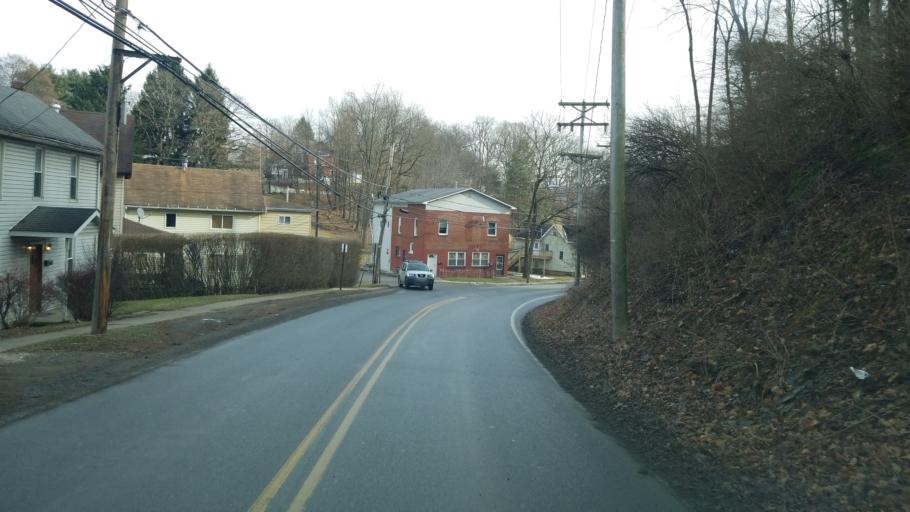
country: US
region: Pennsylvania
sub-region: Jefferson County
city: Punxsutawney
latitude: 40.9485
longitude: -78.9750
